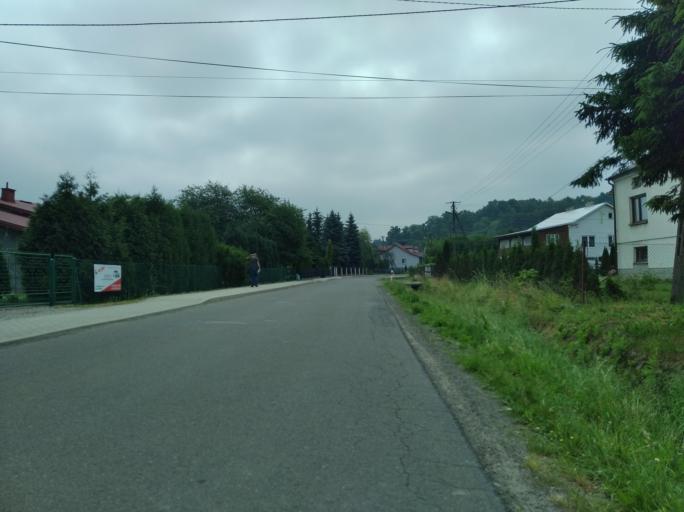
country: PL
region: Subcarpathian Voivodeship
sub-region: Powiat sanocki
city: Besko
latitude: 49.5900
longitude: 21.9449
